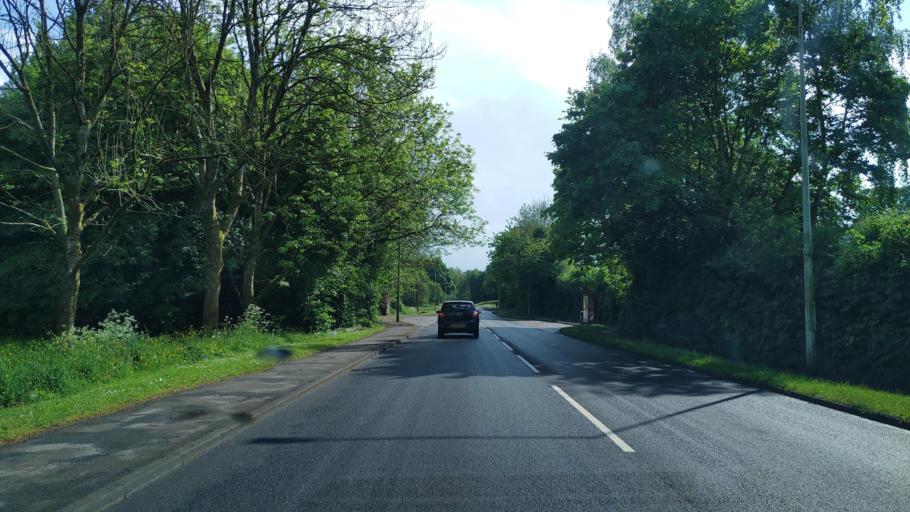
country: GB
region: England
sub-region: Lancashire
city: Clayton-le-Woods
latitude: 53.7090
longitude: -2.6336
